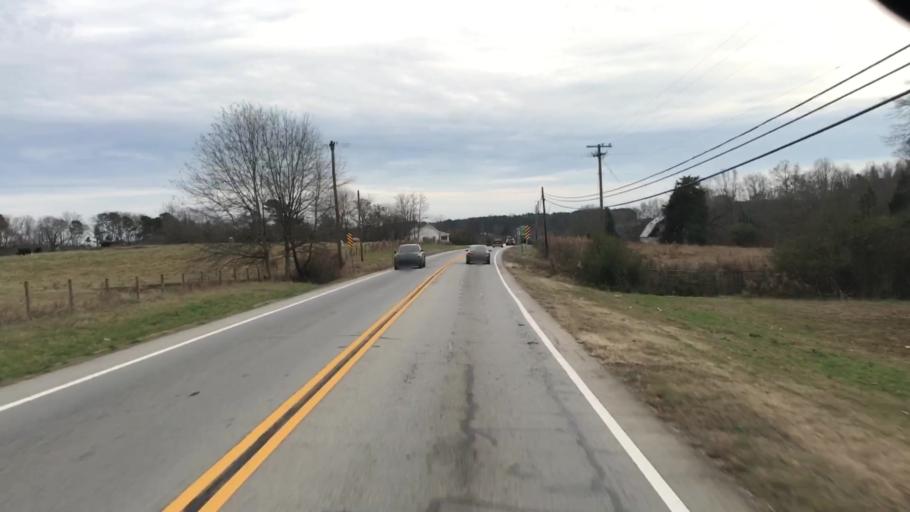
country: US
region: Georgia
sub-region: Barrow County
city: Winder
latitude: 34.0156
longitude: -83.7590
